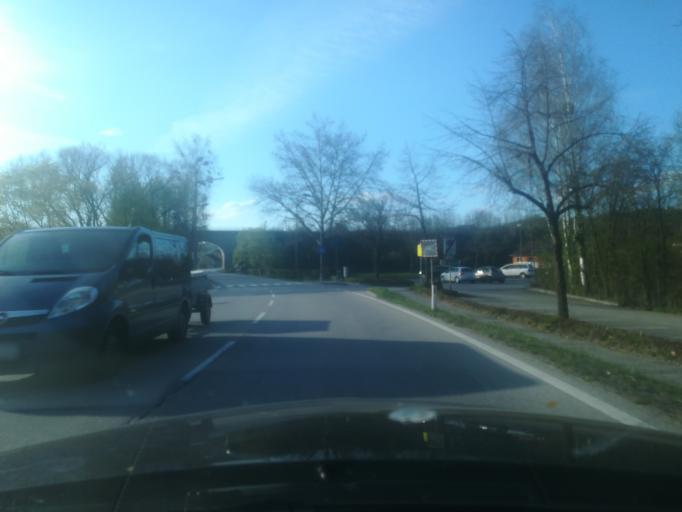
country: AT
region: Upper Austria
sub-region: Politischer Bezirk Perg
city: Bad Kreuzen
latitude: 48.2267
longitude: 14.8487
